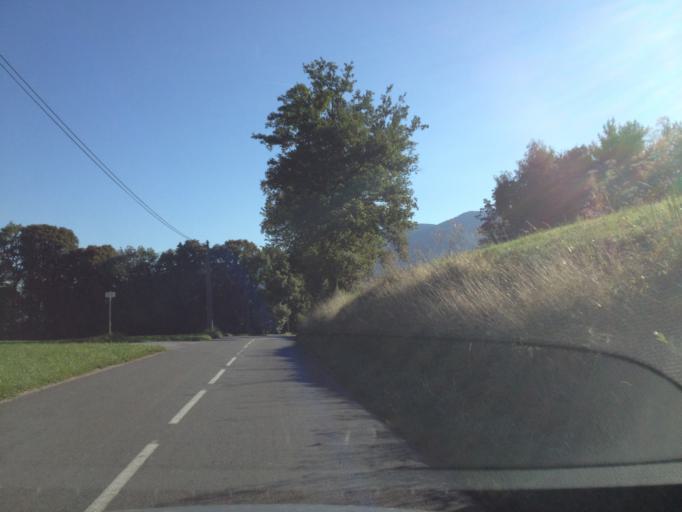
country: FR
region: Rhone-Alpes
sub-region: Departement de la Savoie
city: Gresy-sur-Aix
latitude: 45.7087
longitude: 5.9671
